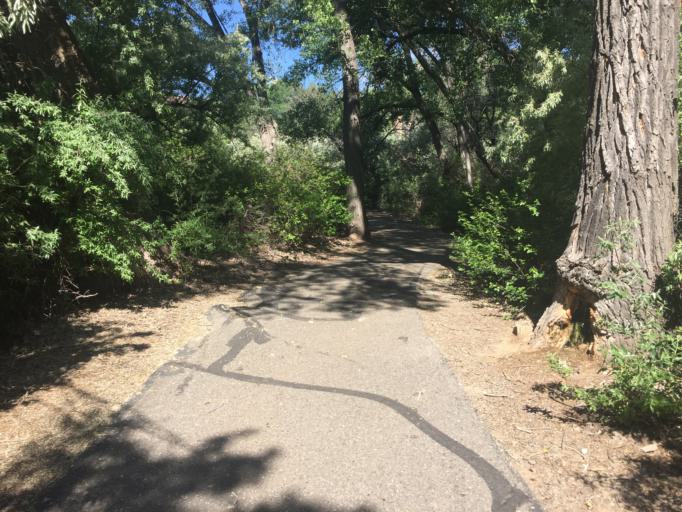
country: US
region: Colorado
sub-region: Mesa County
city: Redlands
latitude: 39.0712
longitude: -108.6003
